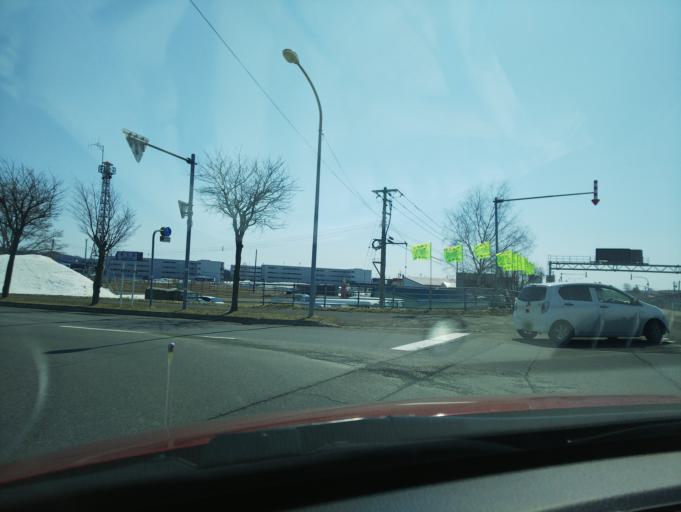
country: JP
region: Hokkaido
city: Nayoro
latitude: 44.1910
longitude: 142.3927
